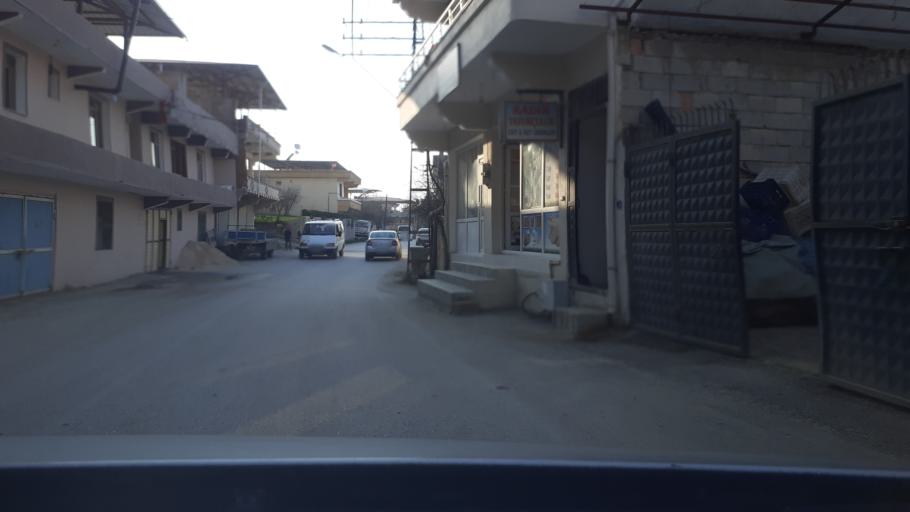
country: TR
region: Hatay
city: Oymakli
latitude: 36.1132
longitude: 36.2965
